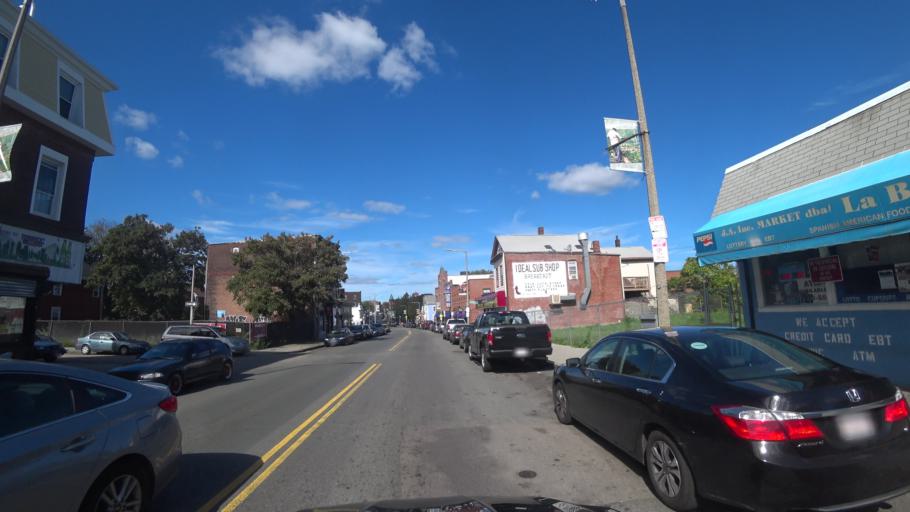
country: US
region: Massachusetts
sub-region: Suffolk County
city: South Boston
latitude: 42.3219
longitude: -71.0724
